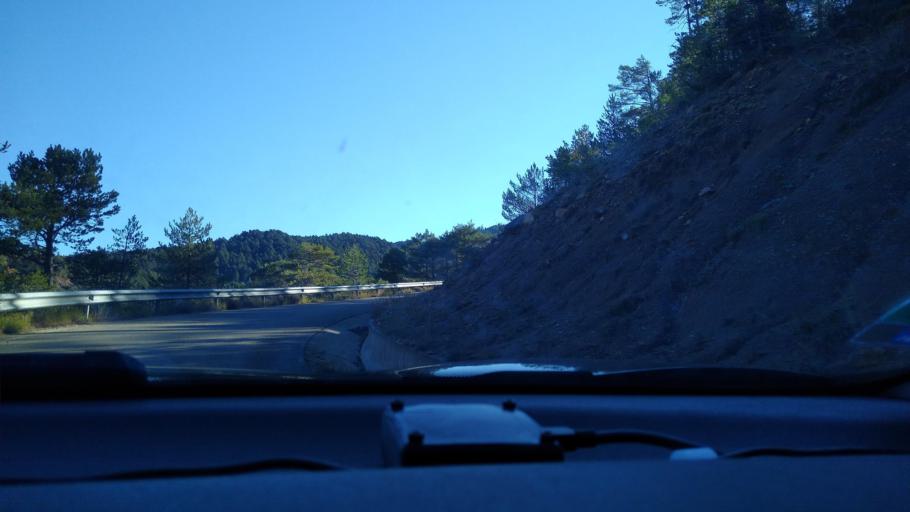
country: ES
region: Catalonia
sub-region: Provincia de Barcelona
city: Saldes
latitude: 42.2082
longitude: 1.7249
